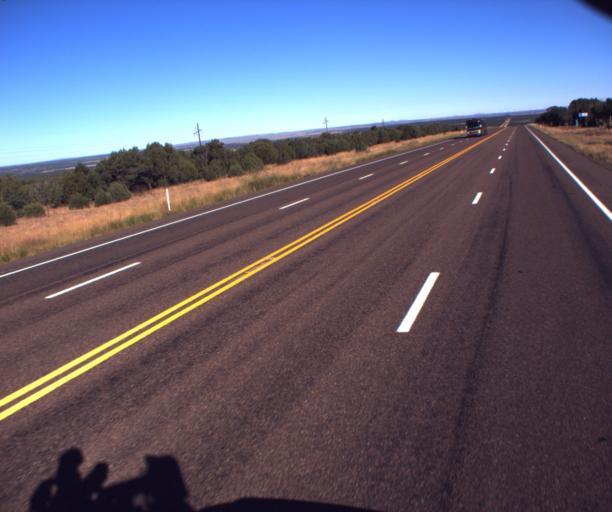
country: US
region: Arizona
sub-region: Navajo County
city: White Mountain Lake
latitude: 34.3357
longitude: -110.0488
